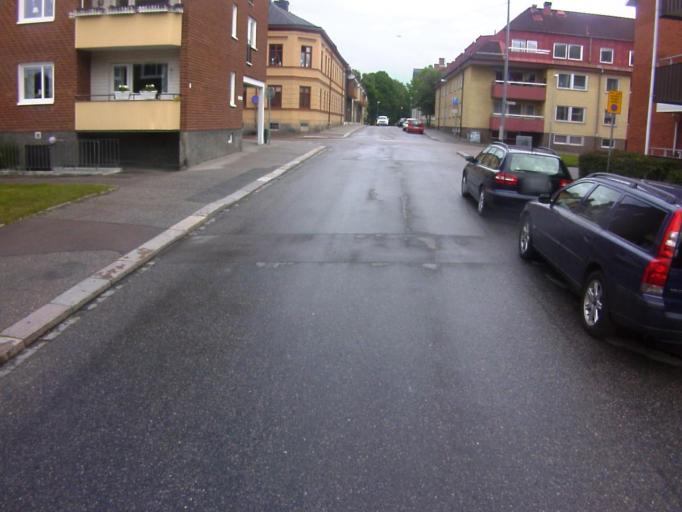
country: SE
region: Soedermanland
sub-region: Eskilstuna Kommun
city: Eskilstuna
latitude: 59.3642
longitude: 16.5166
